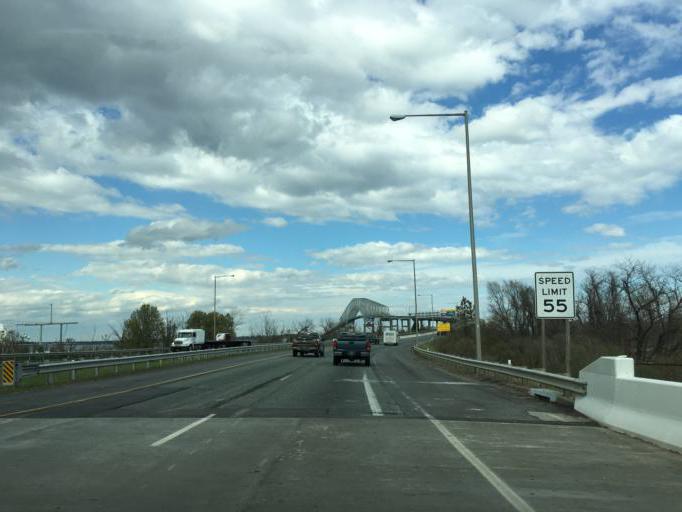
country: US
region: Maryland
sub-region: Baltimore County
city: Dundalk
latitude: 39.2084
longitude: -76.5429
